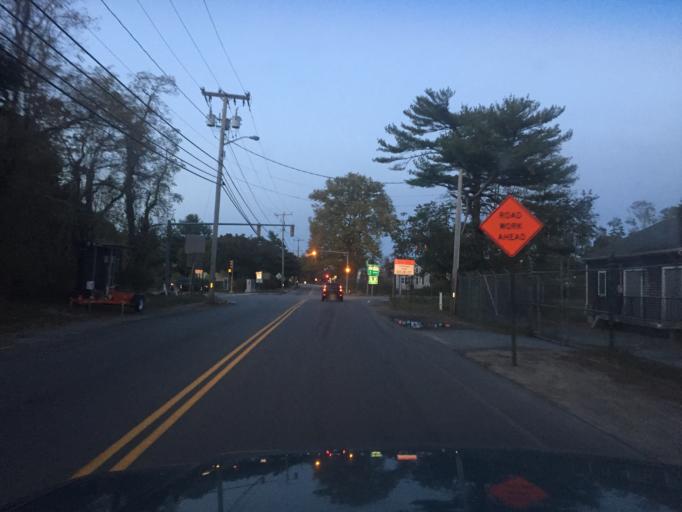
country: US
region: Massachusetts
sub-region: Plymouth County
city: Onset
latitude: 41.7599
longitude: -70.6745
